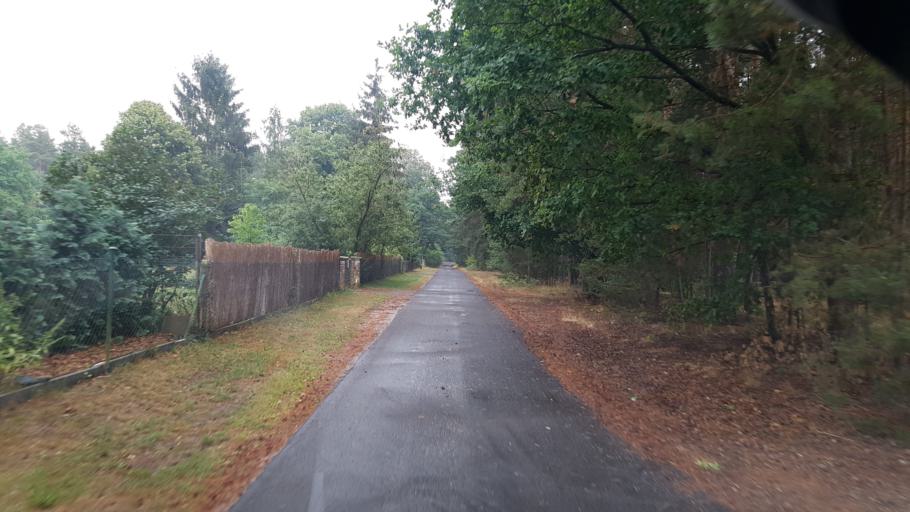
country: DE
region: Brandenburg
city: Finsterwalde
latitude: 51.6448
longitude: 13.7856
